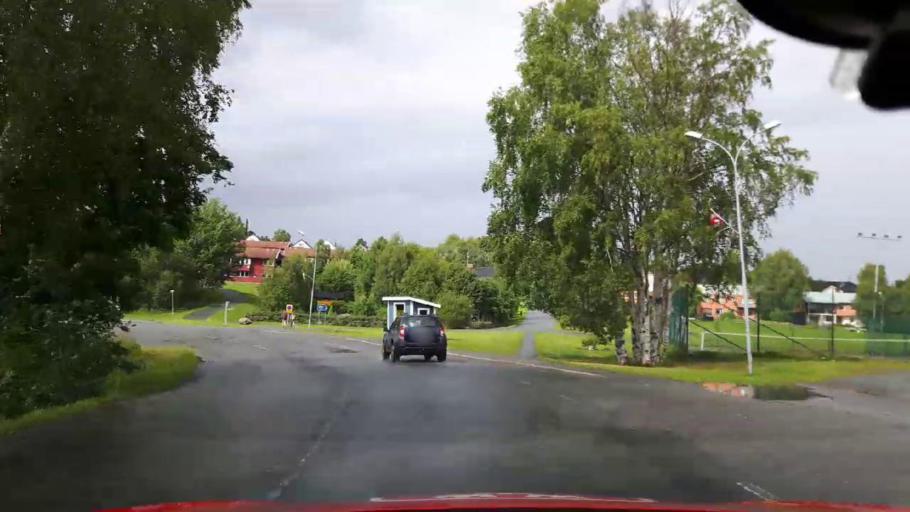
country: SE
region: Jaemtland
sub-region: Krokoms Kommun
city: Krokom
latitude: 63.3503
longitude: 14.2511
